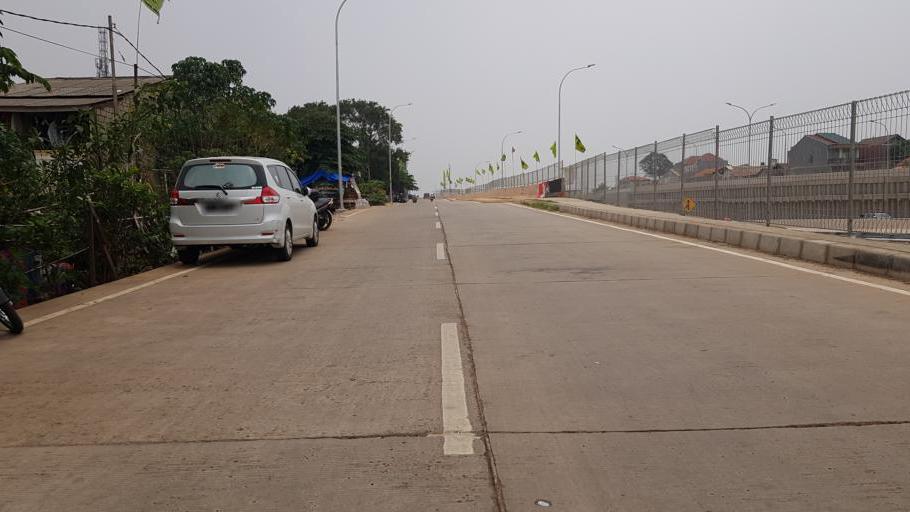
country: ID
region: West Java
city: Pamulang
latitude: -6.3296
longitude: 106.8008
